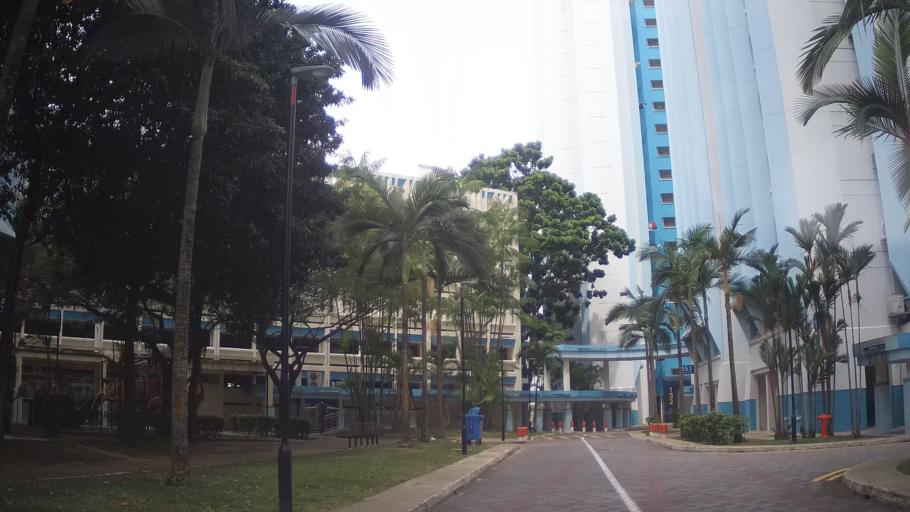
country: MY
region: Johor
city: Johor Bahru
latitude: 1.3751
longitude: 103.7651
